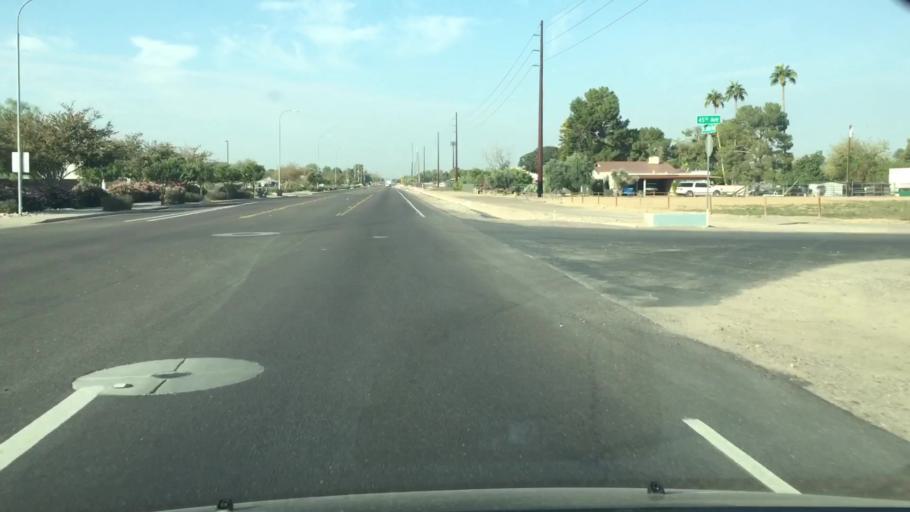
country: US
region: Arizona
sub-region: Maricopa County
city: Laveen
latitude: 33.3630
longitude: -112.1561
